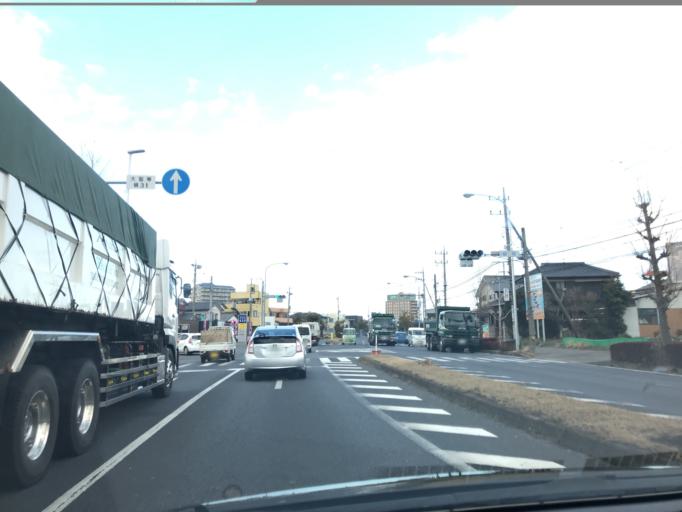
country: JP
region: Ibaraki
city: Mitsukaido
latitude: 36.0126
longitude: 139.9905
